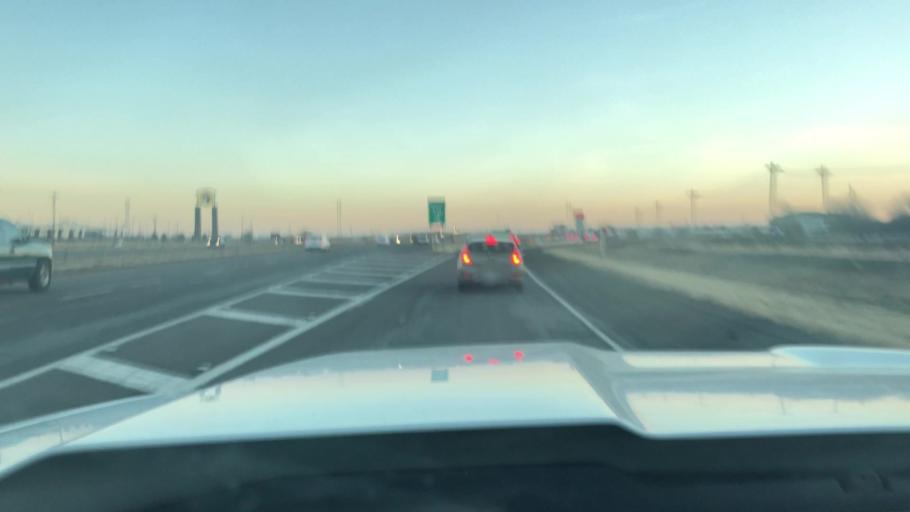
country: US
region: Texas
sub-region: Denton County
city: Roanoke
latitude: 33.0210
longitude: -97.2782
